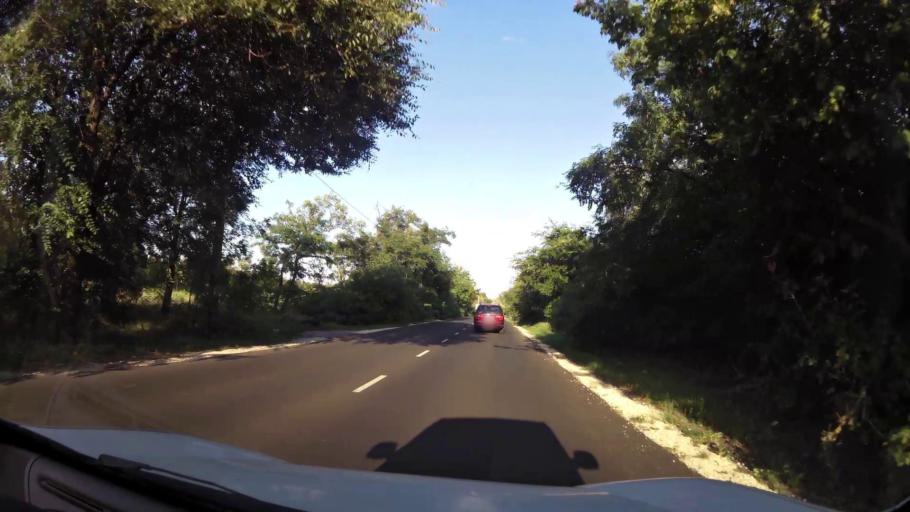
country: HU
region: Budapest
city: Budapest X. keruelet
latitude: 47.4979
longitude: 19.1452
